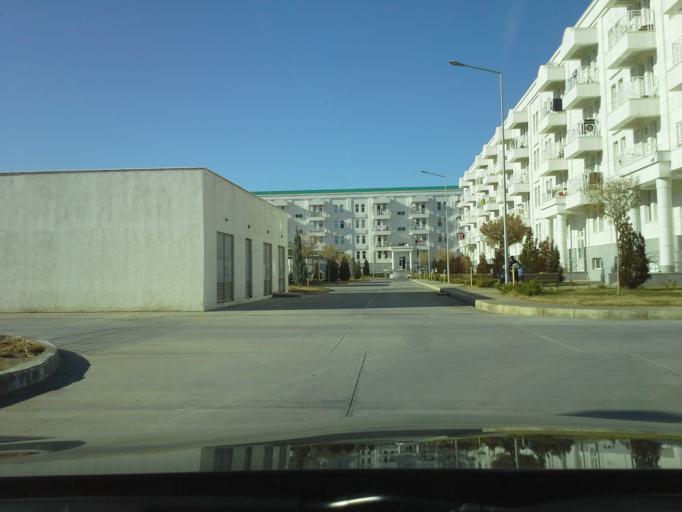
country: TM
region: Ahal
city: Ashgabat
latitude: 37.9694
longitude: 58.3369
